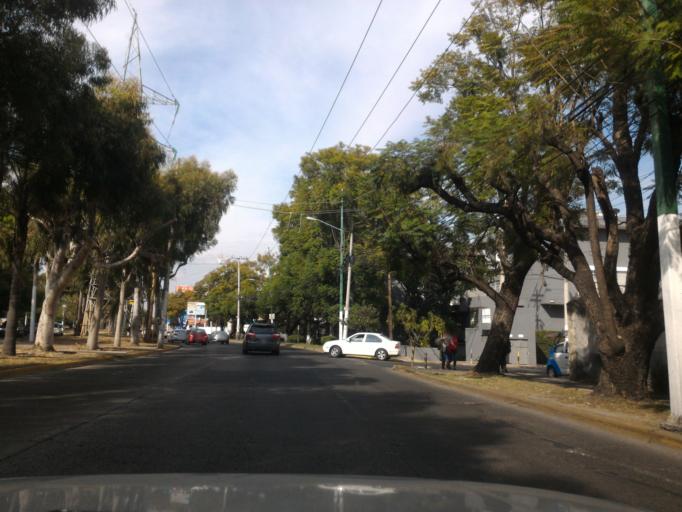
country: MX
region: Jalisco
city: Zapopan2
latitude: 20.6951
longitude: -103.4152
